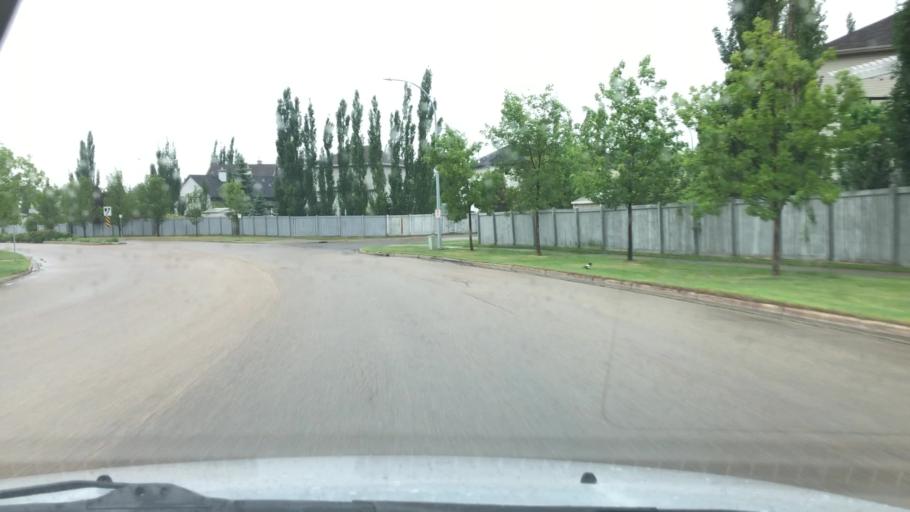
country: CA
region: Alberta
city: Sherwood Park
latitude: 53.5374
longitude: -113.2609
